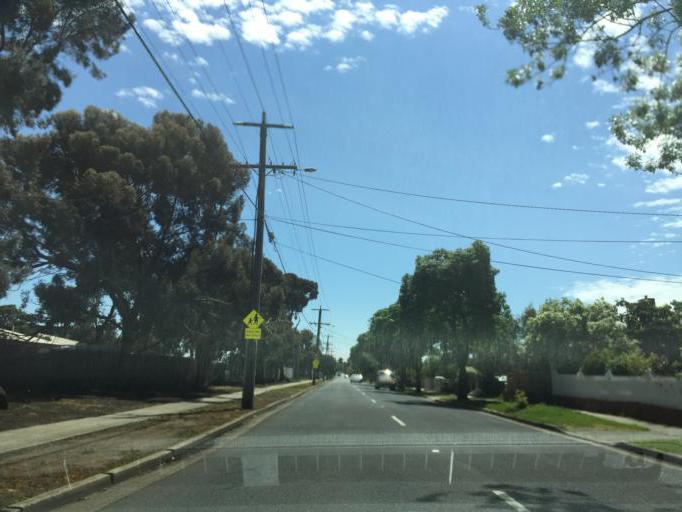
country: AU
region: Victoria
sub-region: Maribyrnong
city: Braybrook
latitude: -37.7855
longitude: 144.8461
